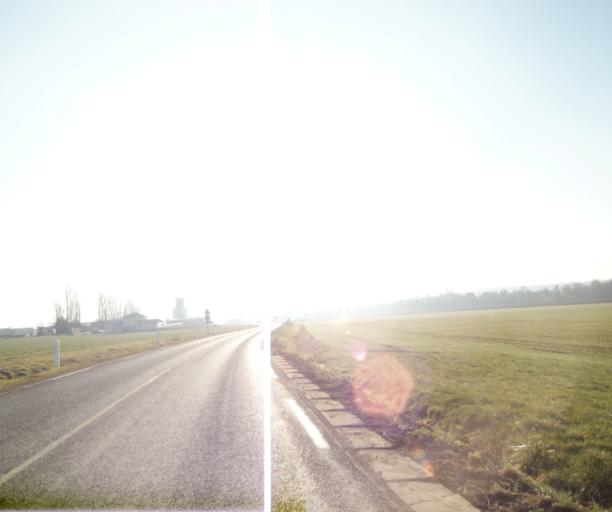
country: FR
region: Champagne-Ardenne
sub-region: Departement de la Haute-Marne
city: Wassy
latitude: 48.5163
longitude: 4.9359
